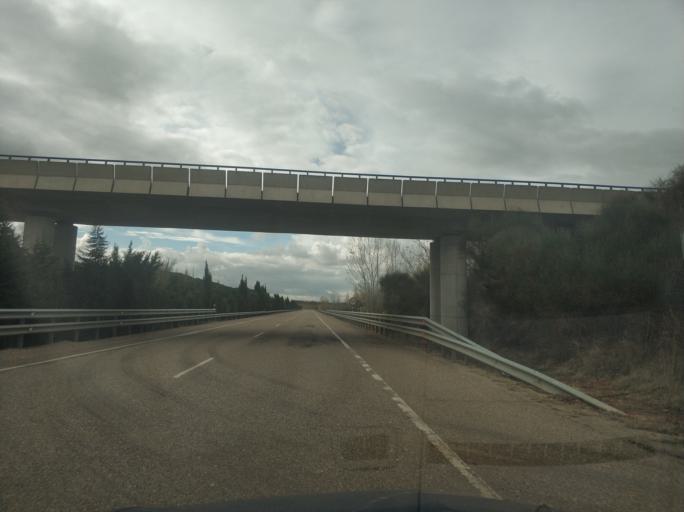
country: ES
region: Castille and Leon
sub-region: Provincia de Valladolid
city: Torrecilla de la Abadesa
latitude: 41.4674
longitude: -5.0667
